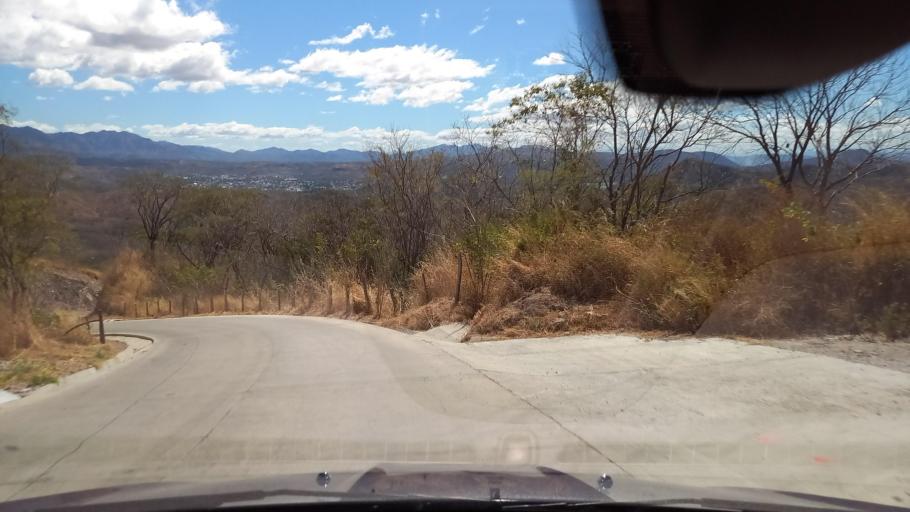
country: SV
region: Santa Ana
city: Metapan
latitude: 14.3657
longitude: -89.4848
